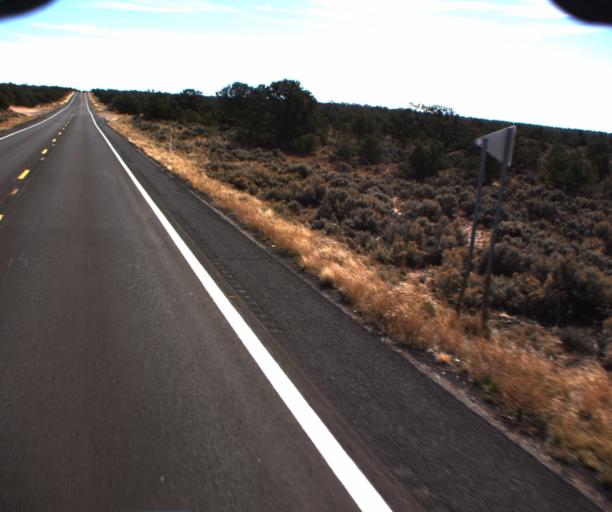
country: US
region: Arizona
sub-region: Coconino County
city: Kaibito
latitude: 36.5903
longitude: -110.8839
